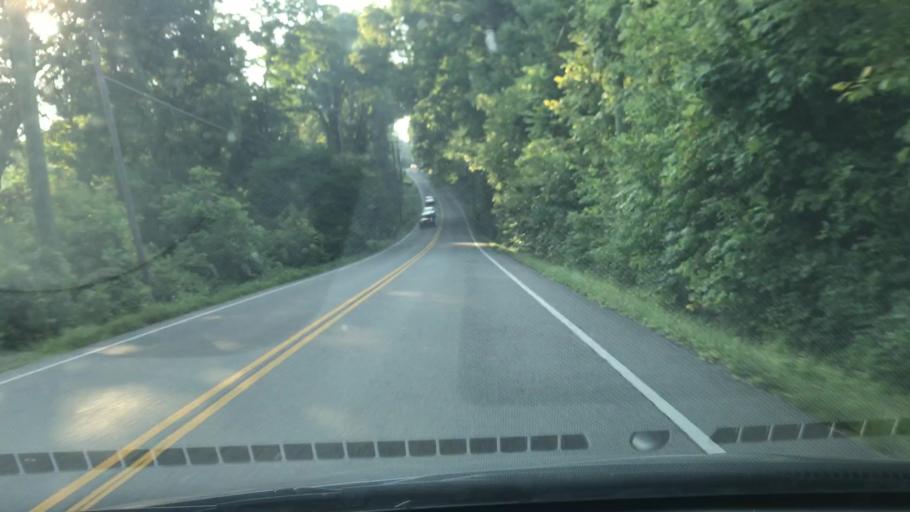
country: US
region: Tennessee
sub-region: Williamson County
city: Nolensville
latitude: 35.9911
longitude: -86.6462
